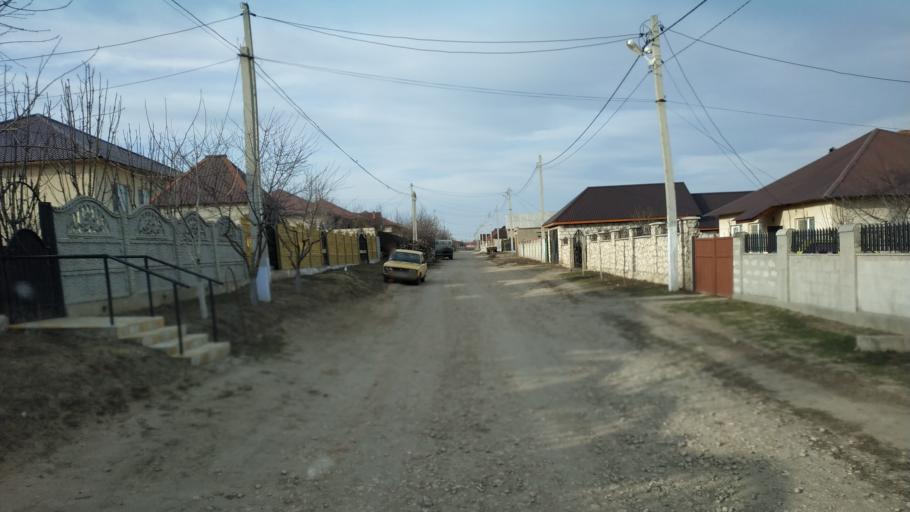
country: RO
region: Vaslui
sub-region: Comuna Dranceni
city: Dranceni
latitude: 46.8411
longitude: 28.1860
